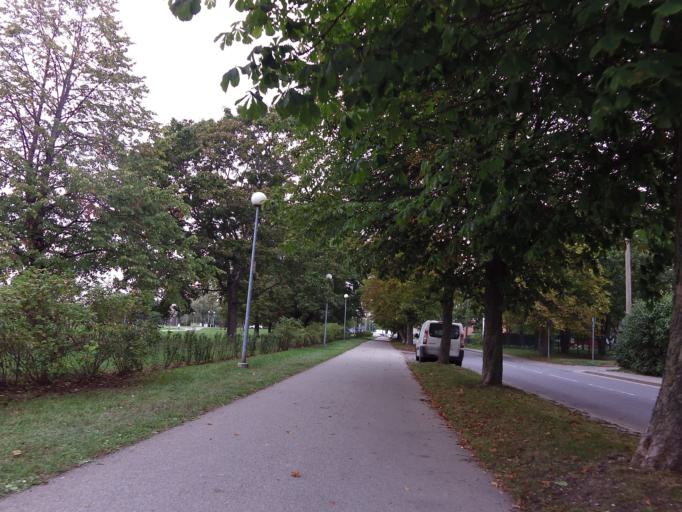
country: EE
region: Harju
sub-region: Tallinna linn
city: Tallinn
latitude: 59.4490
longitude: 24.6864
